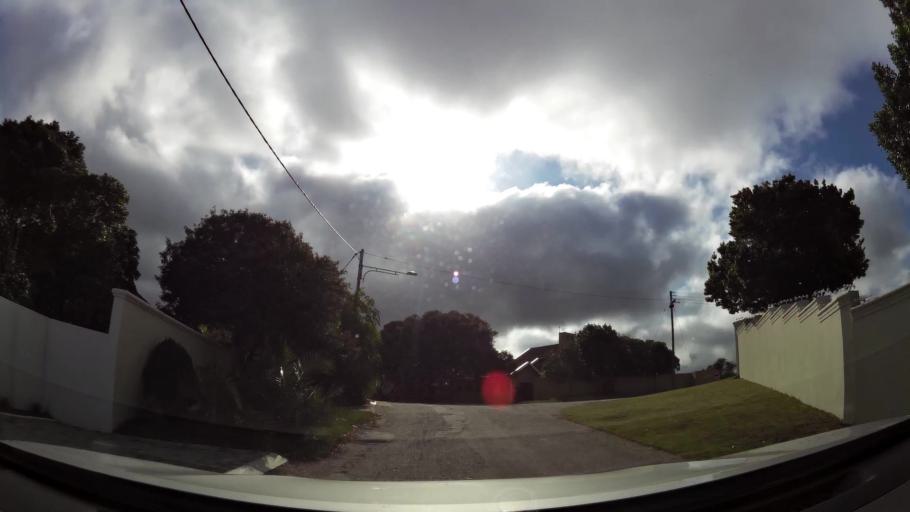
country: ZA
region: Western Cape
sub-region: Eden District Municipality
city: Plettenberg Bay
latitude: -34.0712
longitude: 23.3711
